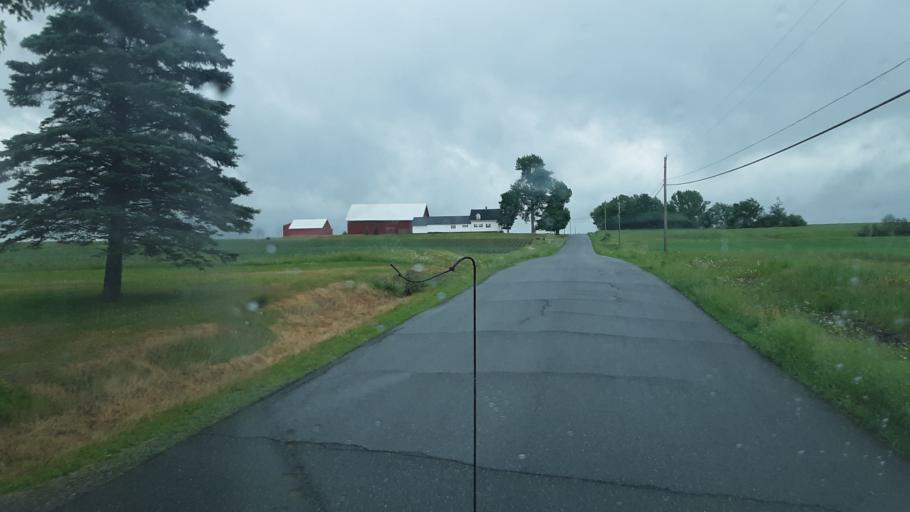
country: US
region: Maine
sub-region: Aroostook County
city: Presque Isle
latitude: 46.6817
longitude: -68.1922
